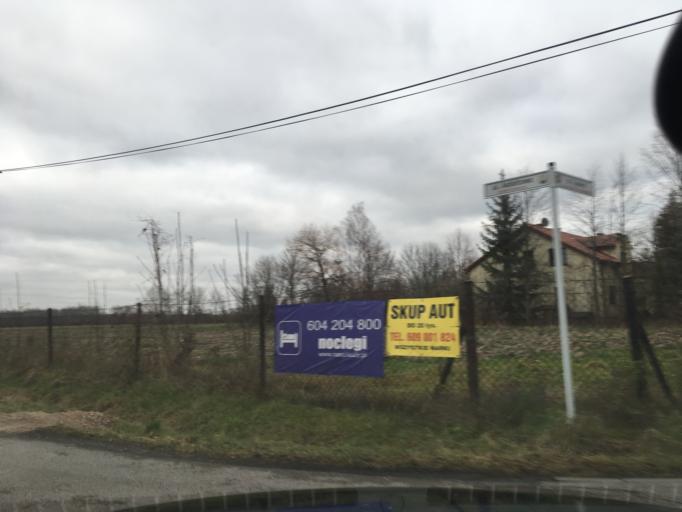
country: PL
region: Masovian Voivodeship
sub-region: Powiat piaseczynski
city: Lesznowola
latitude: 52.0404
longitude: 20.9564
